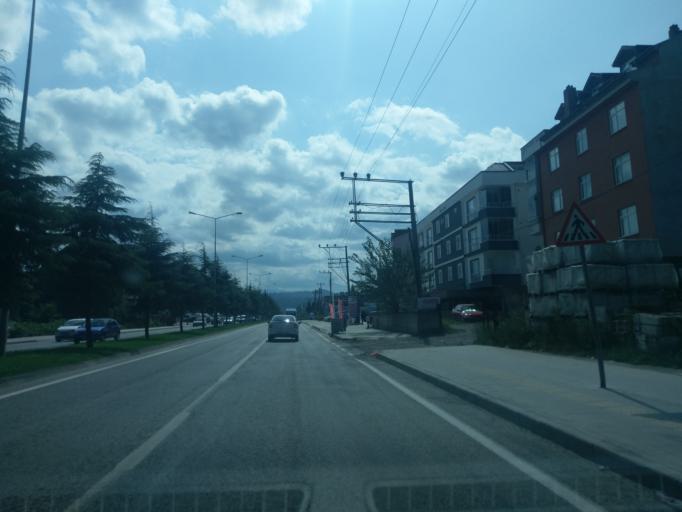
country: TR
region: Ordu
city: Ordu
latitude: 40.9605
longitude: 37.8979
